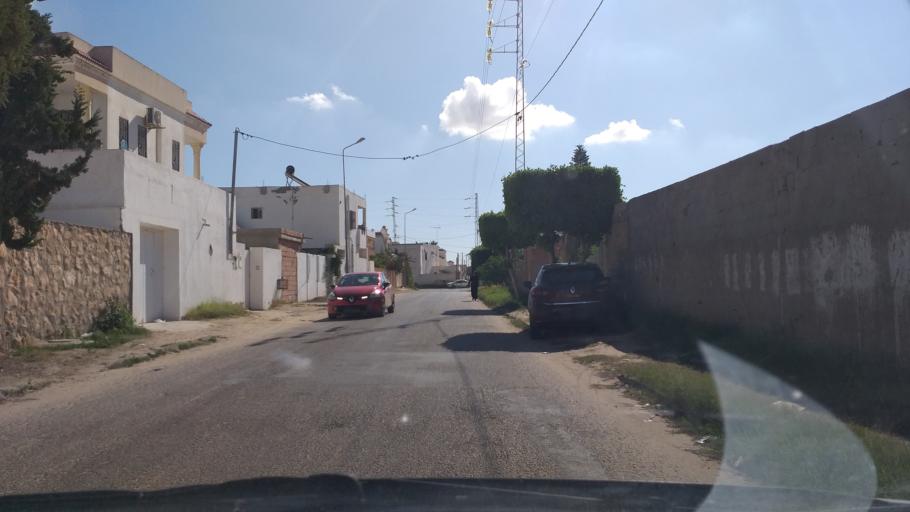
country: TN
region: Safaqis
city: Al Qarmadah
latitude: 34.8008
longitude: 10.7734
